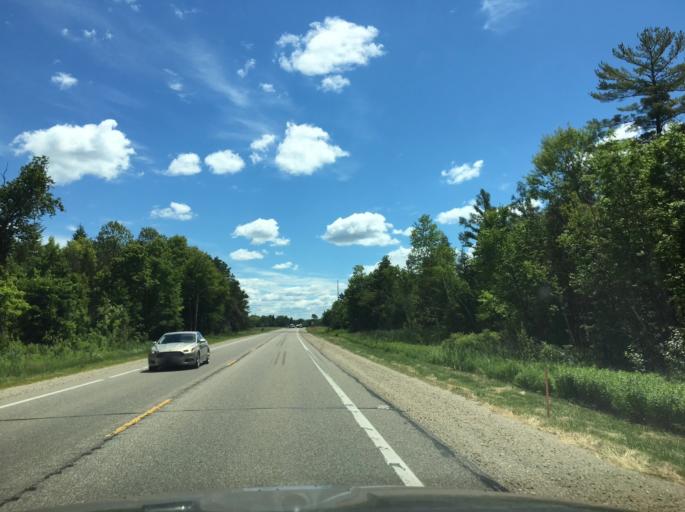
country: US
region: Michigan
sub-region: Osceola County
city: Reed City
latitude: 43.8727
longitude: -85.4087
